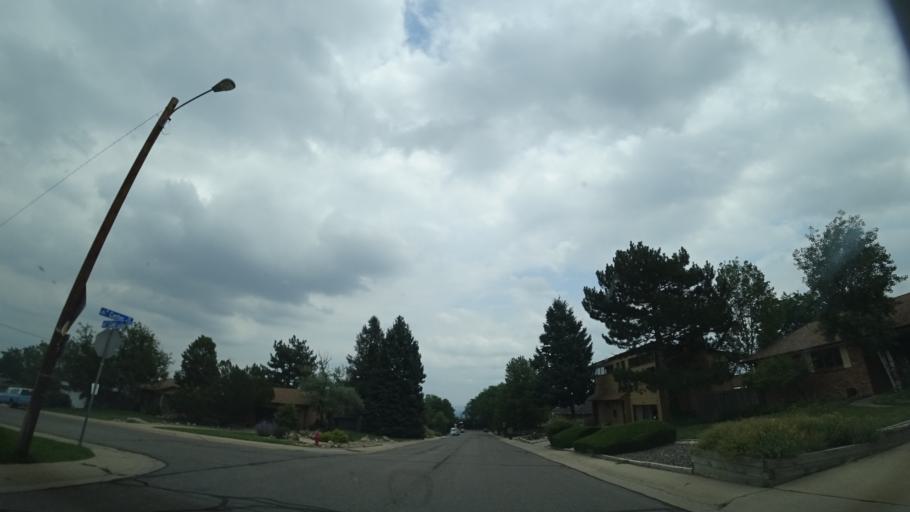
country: US
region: Colorado
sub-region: Jefferson County
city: West Pleasant View
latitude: 39.7042
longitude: -105.1528
